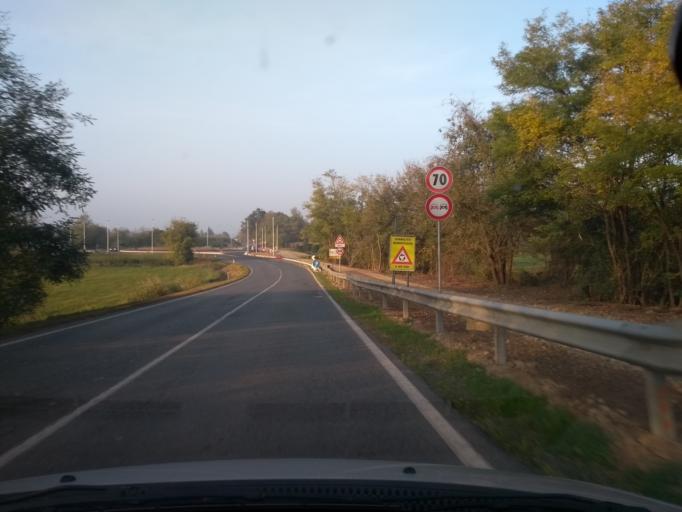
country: IT
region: Piedmont
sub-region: Provincia di Torino
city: San Gillio
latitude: 45.1497
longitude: 7.5353
